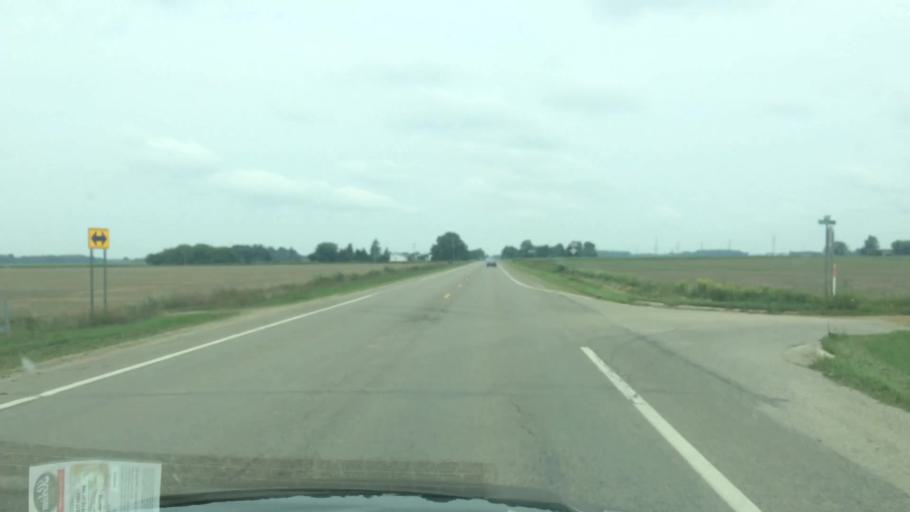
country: US
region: Michigan
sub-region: Huron County
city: Bad Axe
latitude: 43.8451
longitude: -83.0016
